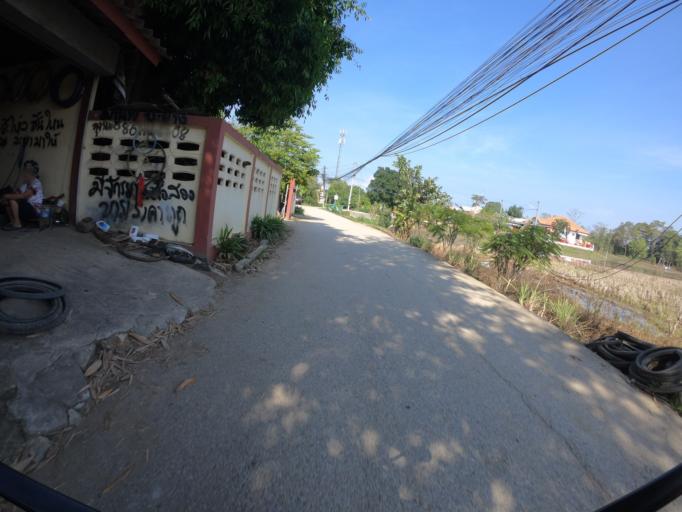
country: TH
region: Chiang Mai
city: San Sai
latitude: 18.8514
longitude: 99.0001
